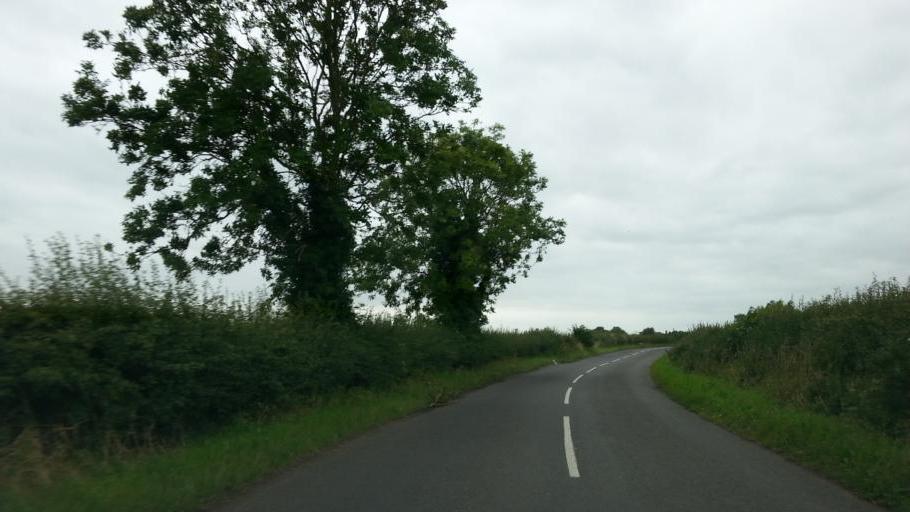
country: GB
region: England
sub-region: Nottinghamshire
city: Newark on Trent
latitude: 53.1029
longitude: -0.8271
